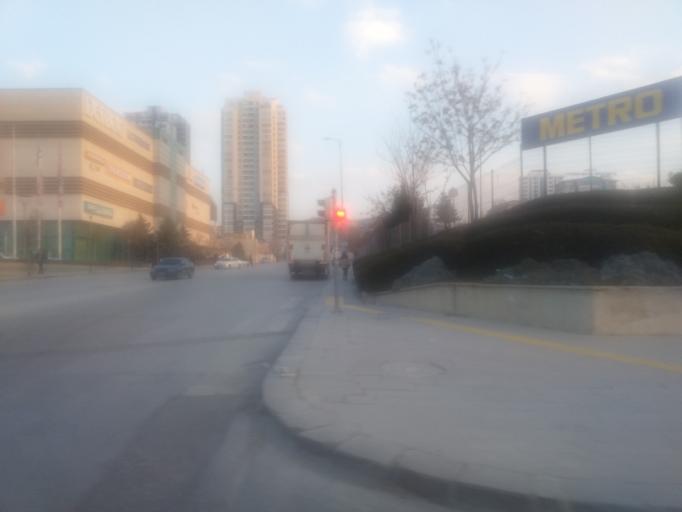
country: TR
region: Ankara
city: Ankara
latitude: 39.9691
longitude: 32.8234
